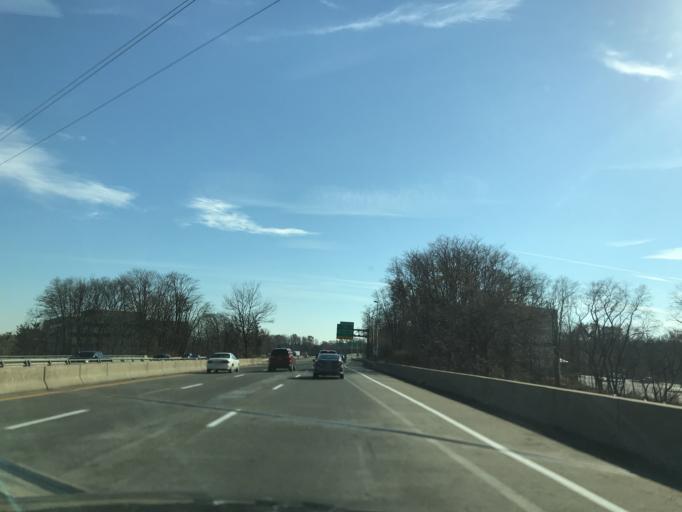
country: US
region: New Jersey
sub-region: Morris County
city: Parsippany
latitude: 40.8711
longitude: -74.4197
